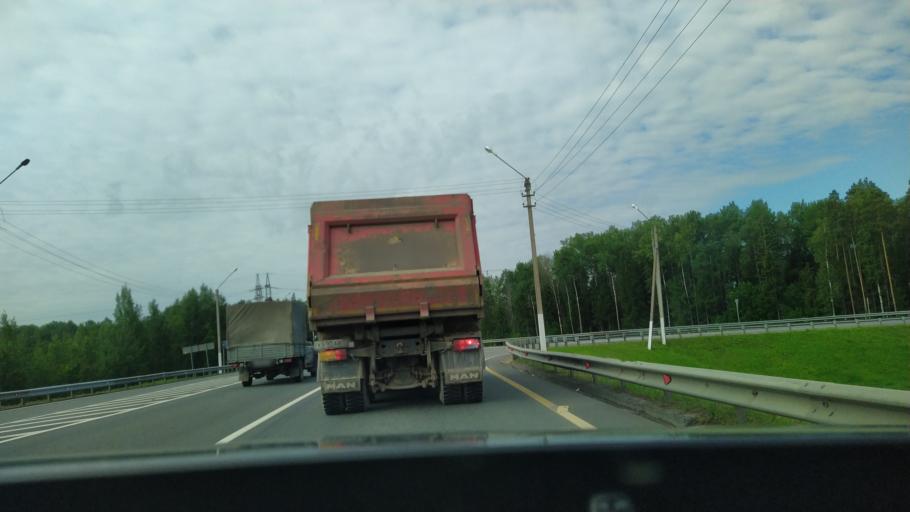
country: RU
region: Leningrad
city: Ul'yanovka
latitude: 59.6046
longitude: 30.7568
